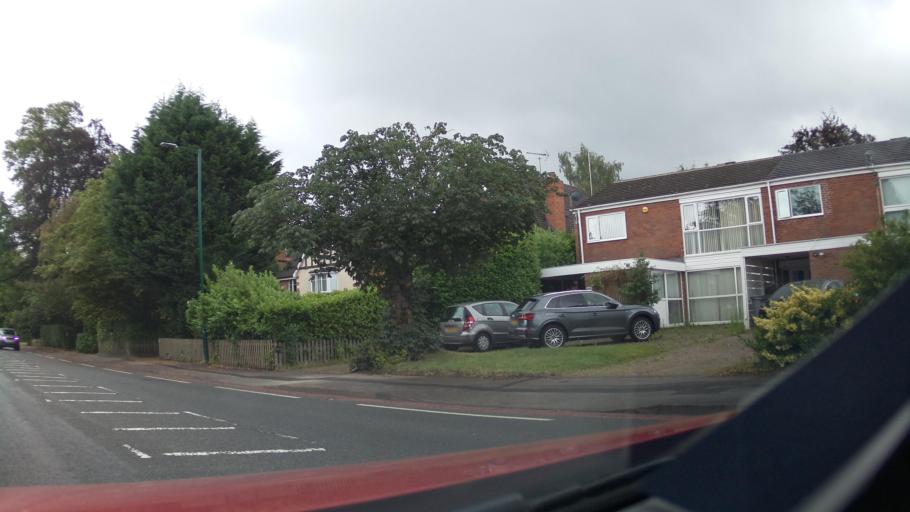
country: GB
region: England
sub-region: Solihull
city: Shirley
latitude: 52.4053
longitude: -1.8034
